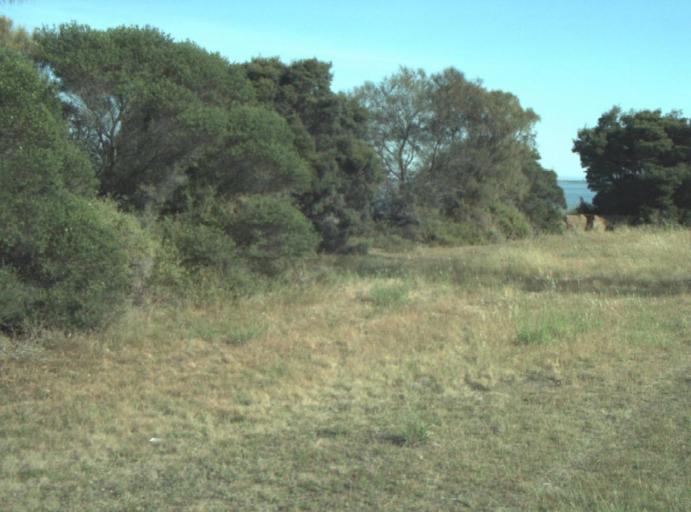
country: AU
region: Victoria
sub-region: Greater Geelong
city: East Geelong
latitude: -38.1349
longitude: 144.4207
